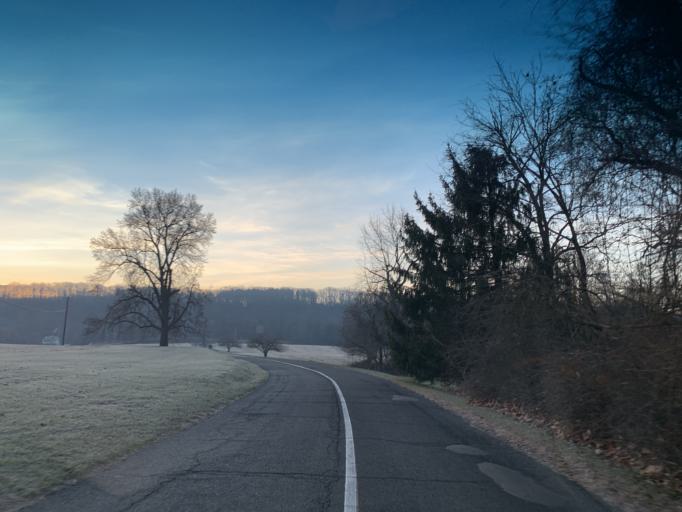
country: US
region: Maryland
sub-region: Baltimore County
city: Carney
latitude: 39.4448
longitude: -76.5170
